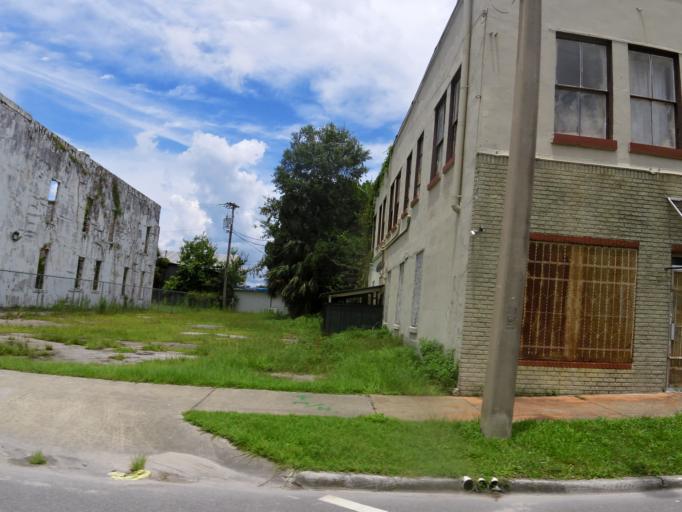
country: US
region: Florida
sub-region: Putnam County
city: East Palatka
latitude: 29.7186
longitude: -81.5084
